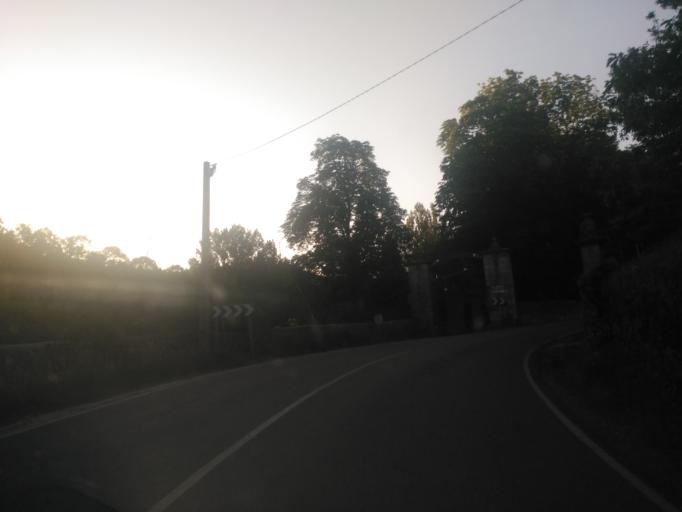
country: ES
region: Castille and Leon
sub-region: Provincia de Salamanca
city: Bejar
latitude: 40.3836
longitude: -5.7559
